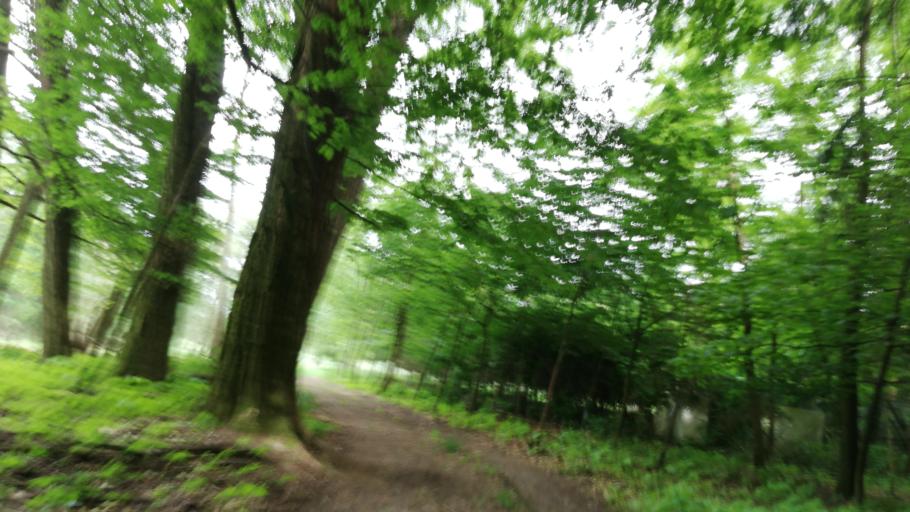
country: AT
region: Upper Austria
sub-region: Wels-Land
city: Gunskirchen
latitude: 48.1721
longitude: 13.9412
